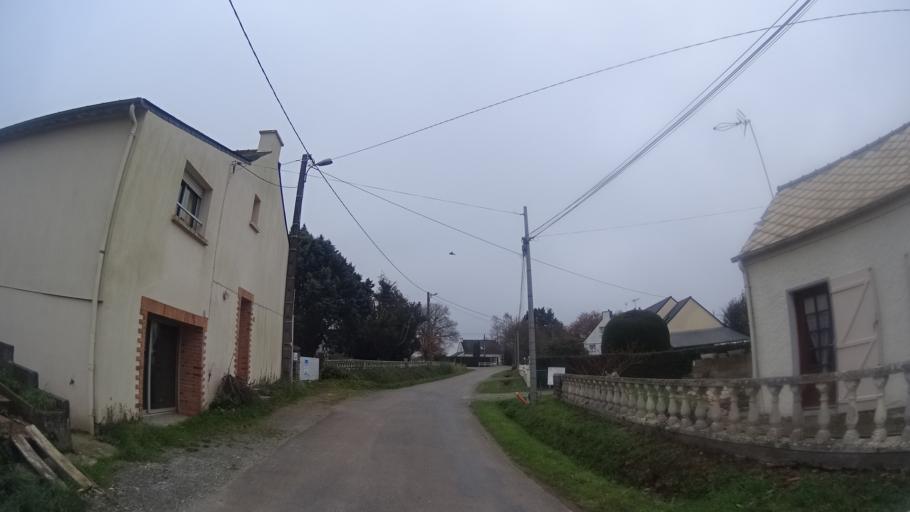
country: FR
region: Brittany
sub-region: Departement du Morbihan
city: Saint-Perreux
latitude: 47.6750
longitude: -2.1119
